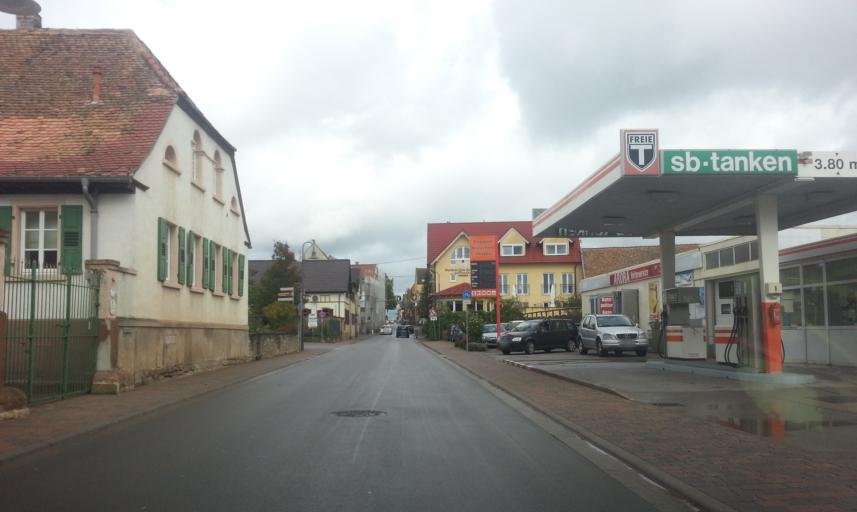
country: DE
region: Rheinland-Pfalz
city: Herxheim am Berg
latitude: 49.5087
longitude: 8.1795
